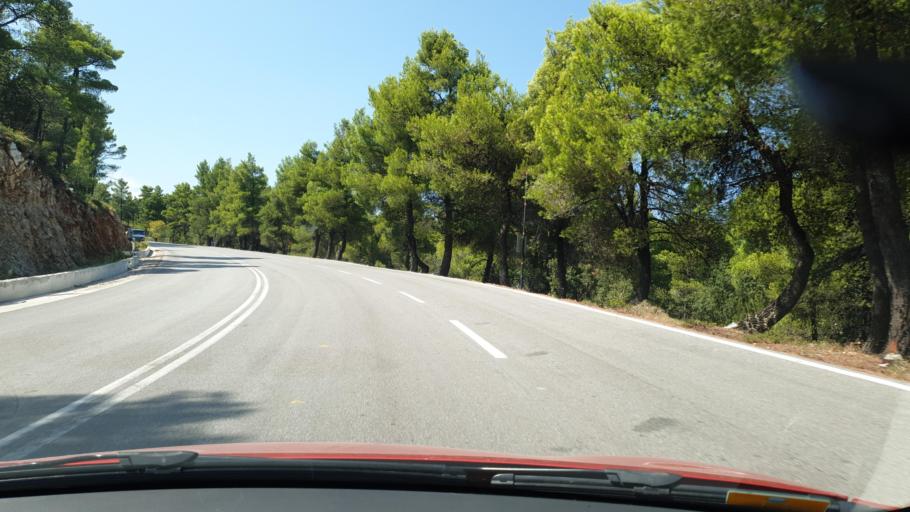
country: GR
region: Central Greece
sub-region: Nomos Evvoias
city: Politika
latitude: 38.6488
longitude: 23.5660
